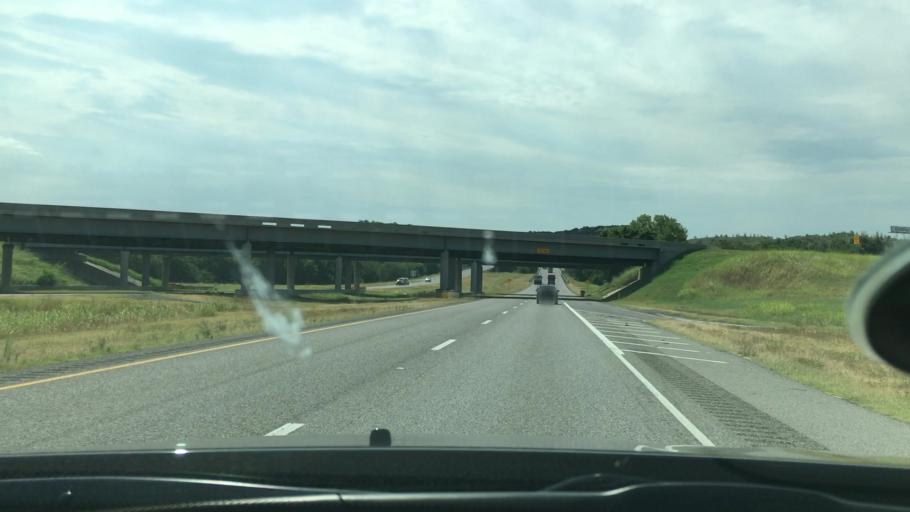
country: US
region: Oklahoma
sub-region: Murray County
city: Davis
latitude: 34.4513
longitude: -97.1362
